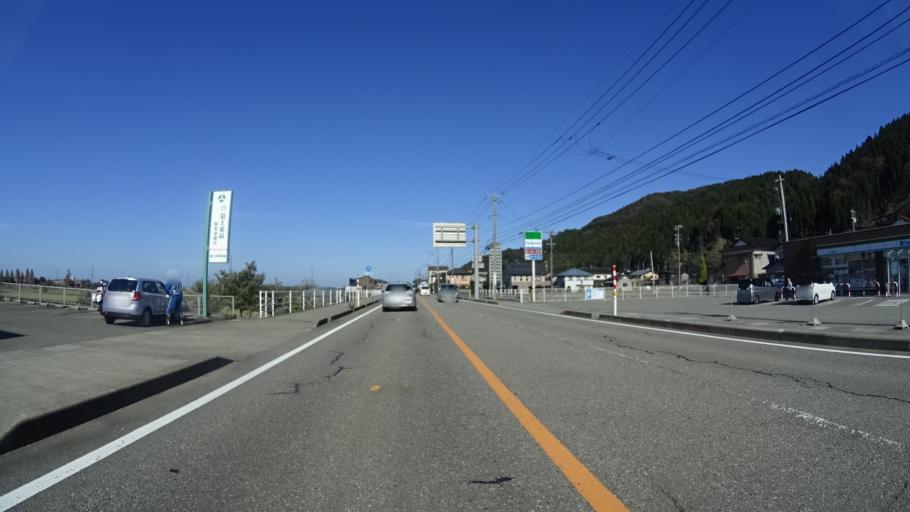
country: JP
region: Ishikawa
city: Tsurugi-asahimachi
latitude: 36.4577
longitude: 136.6225
